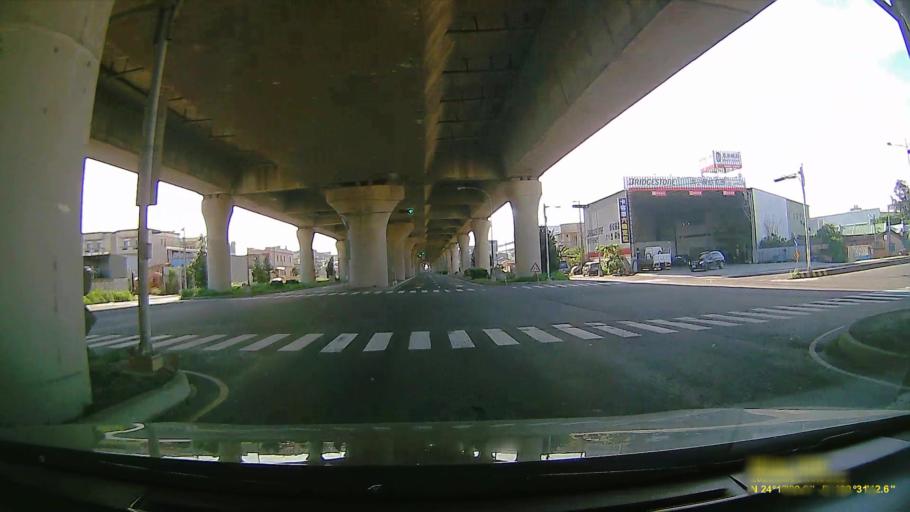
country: TW
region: Taiwan
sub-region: Changhua
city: Chang-hua
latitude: 24.2250
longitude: 120.5198
